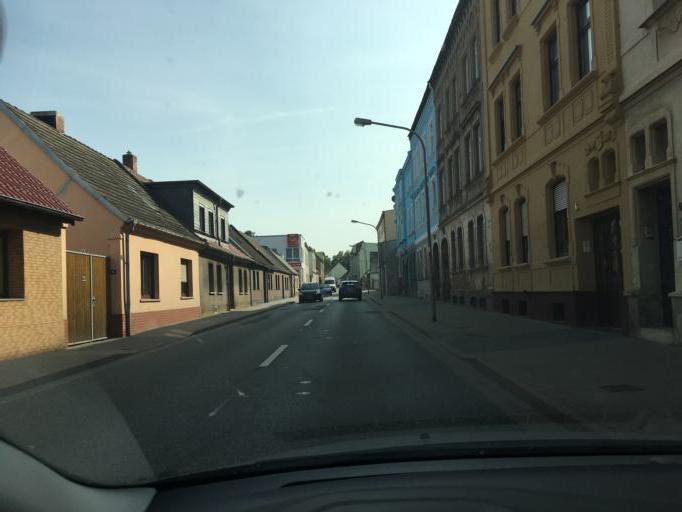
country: DE
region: Saxony-Anhalt
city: Calbe
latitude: 51.9035
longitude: 11.7712
